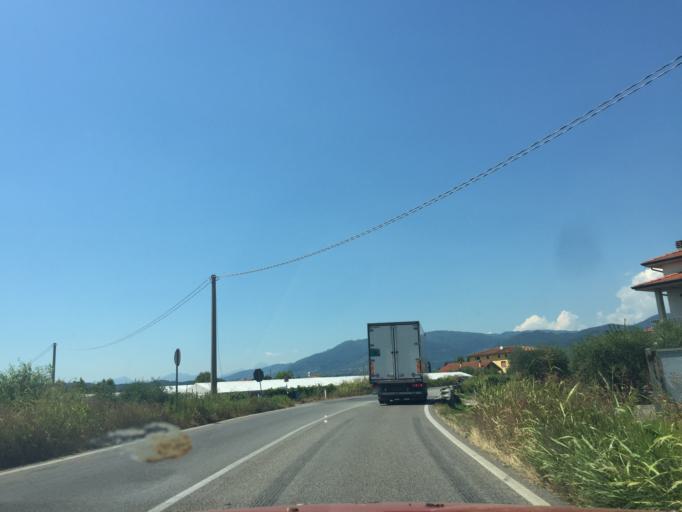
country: IT
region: Tuscany
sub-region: Provincia di Pistoia
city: Chiesina Uzzanese
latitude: 43.8544
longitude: 10.7049
